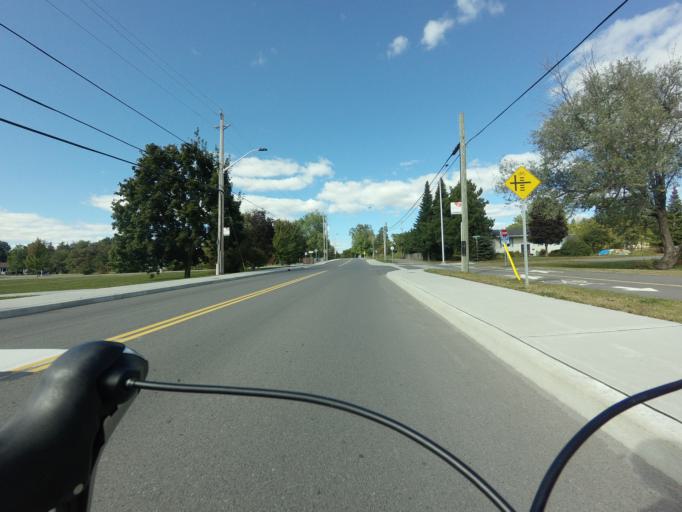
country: CA
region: Ontario
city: Bells Corners
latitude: 45.1529
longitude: -75.6483
